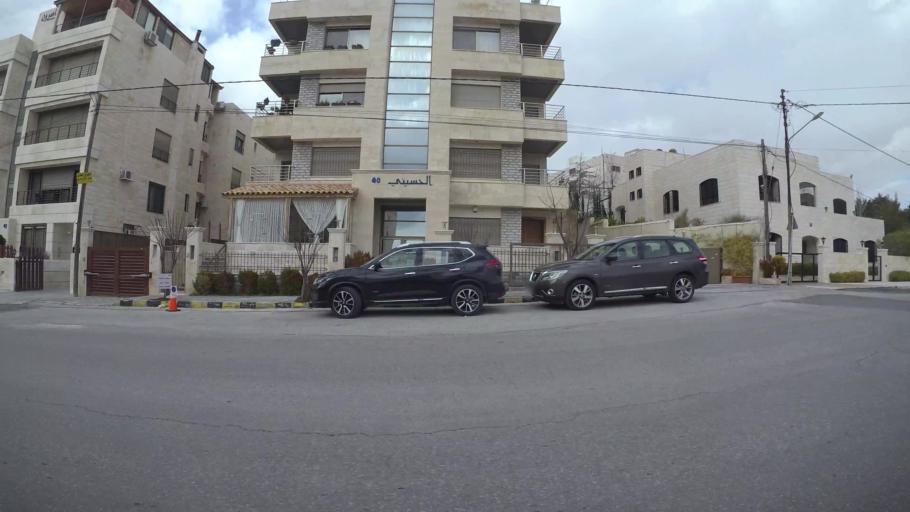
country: JO
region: Amman
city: Wadi as Sir
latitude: 31.9851
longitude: 35.8419
